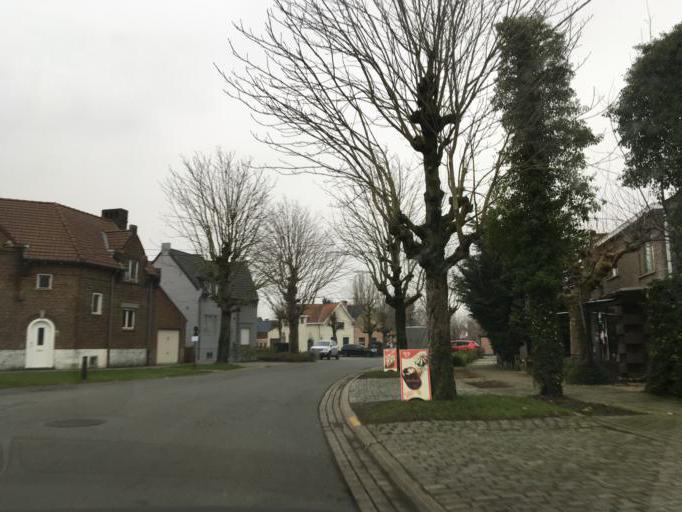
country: BE
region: Flanders
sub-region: Provincie West-Vlaanderen
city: Roeselare
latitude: 50.9510
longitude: 3.1428
